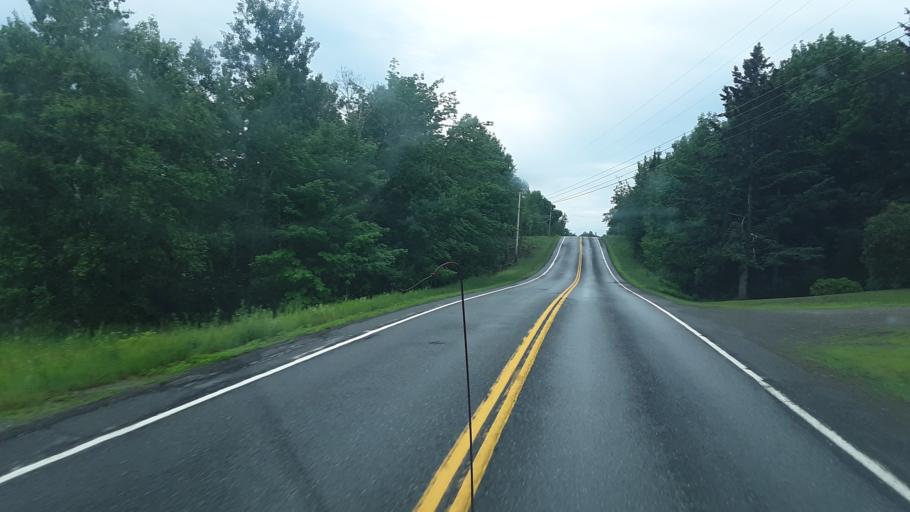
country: US
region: Maine
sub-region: Penobscot County
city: Patten
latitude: 46.0854
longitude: -68.4290
